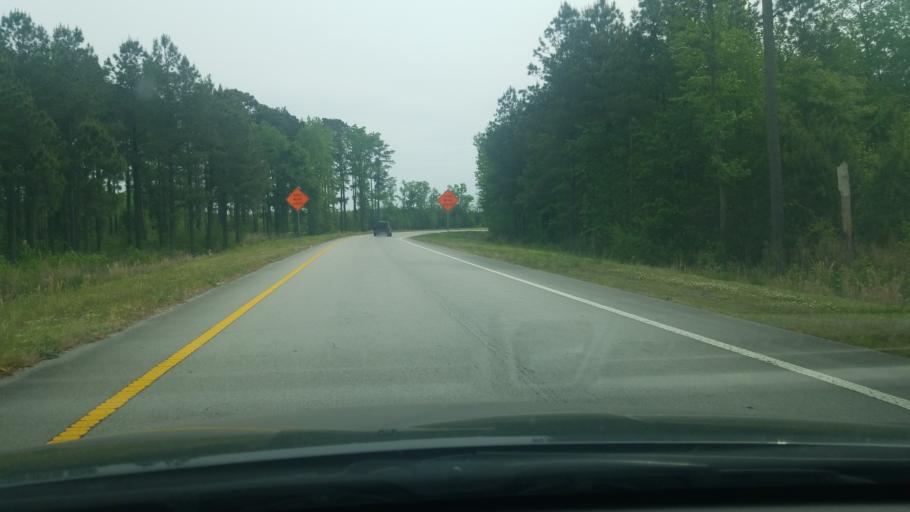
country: US
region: North Carolina
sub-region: Craven County
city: River Bend
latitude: 35.1302
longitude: -77.1501
